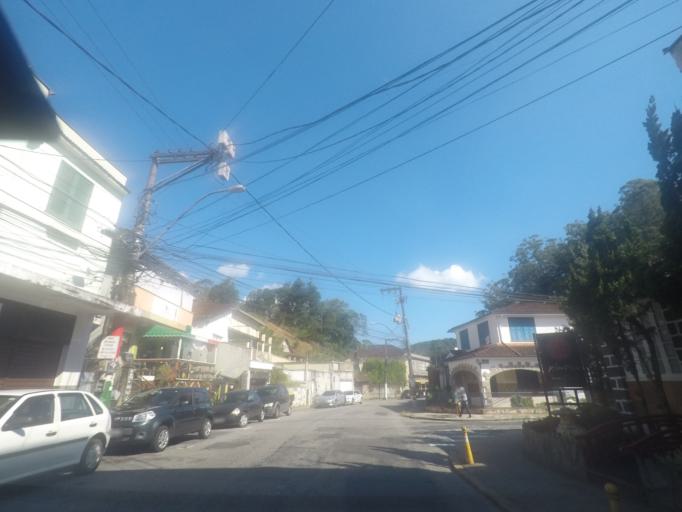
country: BR
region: Rio de Janeiro
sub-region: Petropolis
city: Petropolis
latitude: -22.5188
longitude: -43.1910
